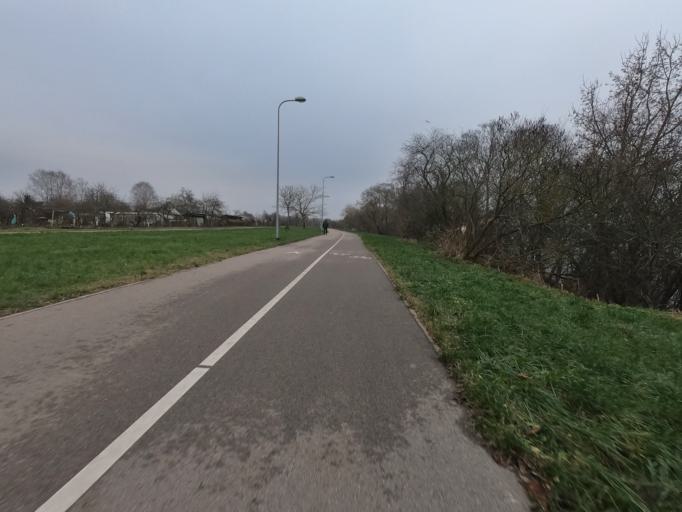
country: LV
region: Kekava
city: Kekava
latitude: 56.8812
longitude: 24.2157
